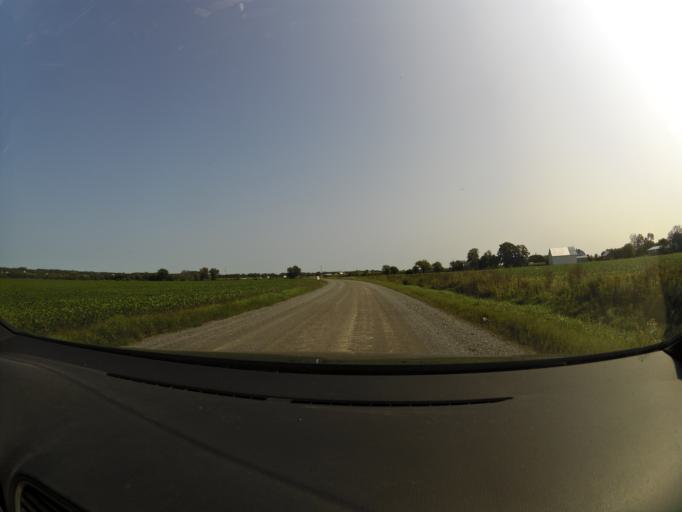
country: CA
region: Ontario
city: Carleton Place
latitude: 45.3463
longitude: -76.0740
